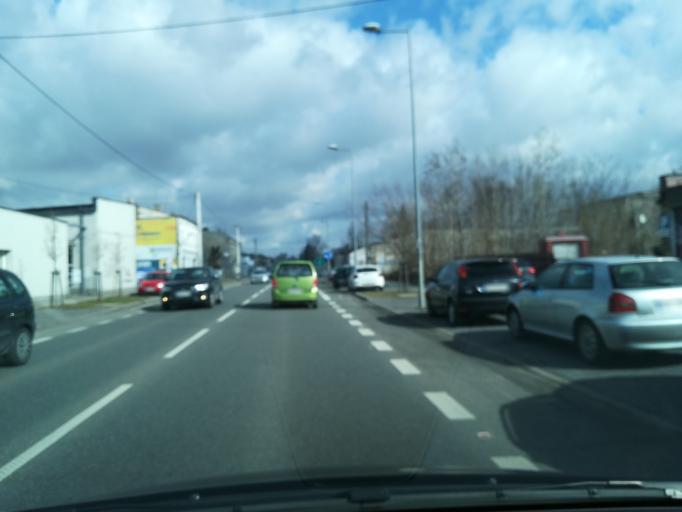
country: PL
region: Silesian Voivodeship
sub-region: Czestochowa
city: Czestochowa
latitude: 50.8221
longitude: 19.1327
